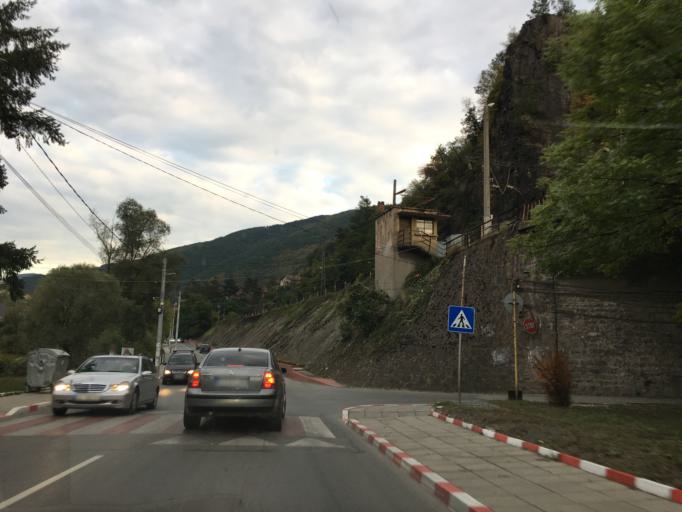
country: BG
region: Sofiya
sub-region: Obshtina Svoge
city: Svoge
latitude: 42.9590
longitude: 23.3544
